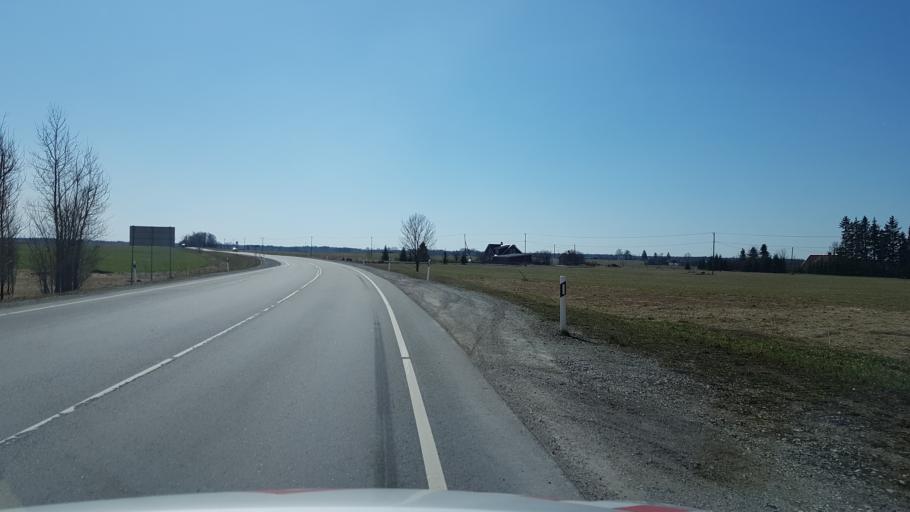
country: EE
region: Ida-Virumaa
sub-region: Kohtla-Jaerve linn
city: Kohtla-Jarve
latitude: 59.3555
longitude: 27.2399
